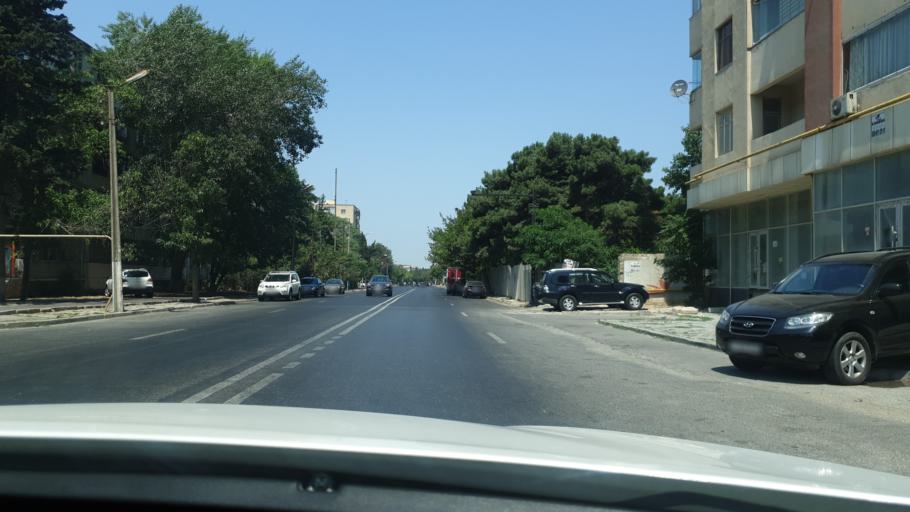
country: AZ
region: Baki
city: Bakixanov
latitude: 40.4151
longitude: 49.9480
